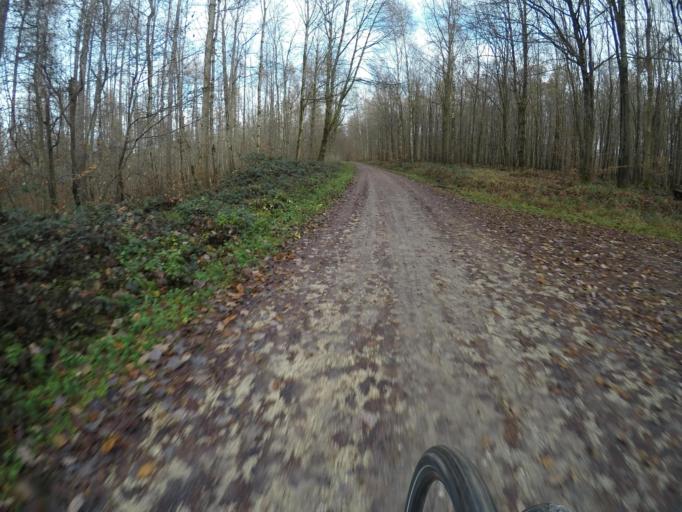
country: DE
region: Baden-Wuerttemberg
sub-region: Regierungsbezirk Stuttgart
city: Baltmannsweiler
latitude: 48.7457
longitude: 9.4222
